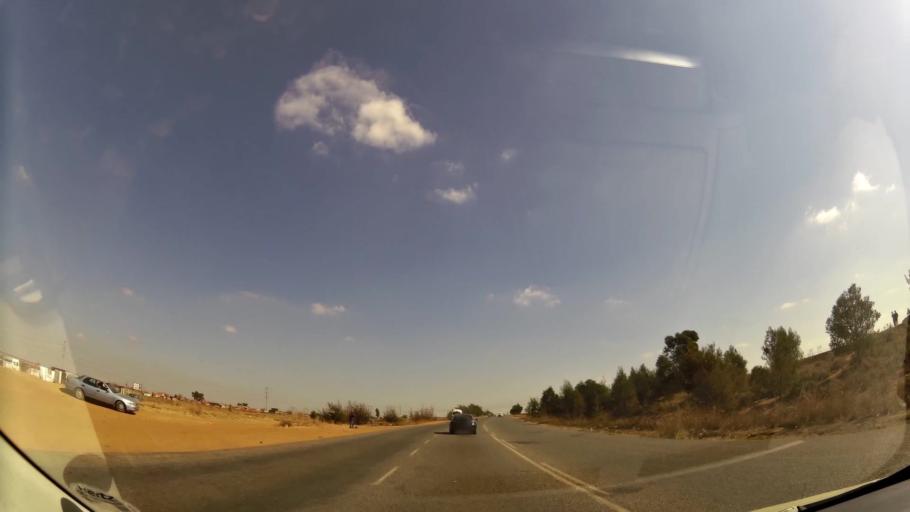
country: ZA
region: Gauteng
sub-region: West Rand District Municipality
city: Randfontein
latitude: -26.1802
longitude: 27.7578
